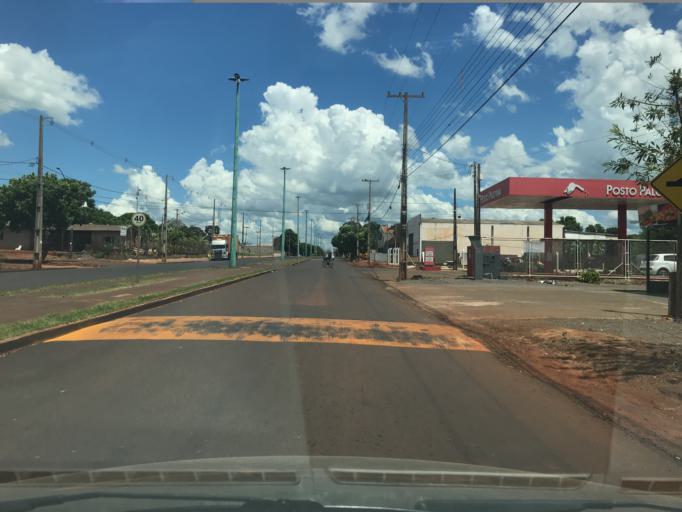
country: BR
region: Parana
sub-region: Palotina
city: Palotina
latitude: -24.2701
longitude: -53.8417
